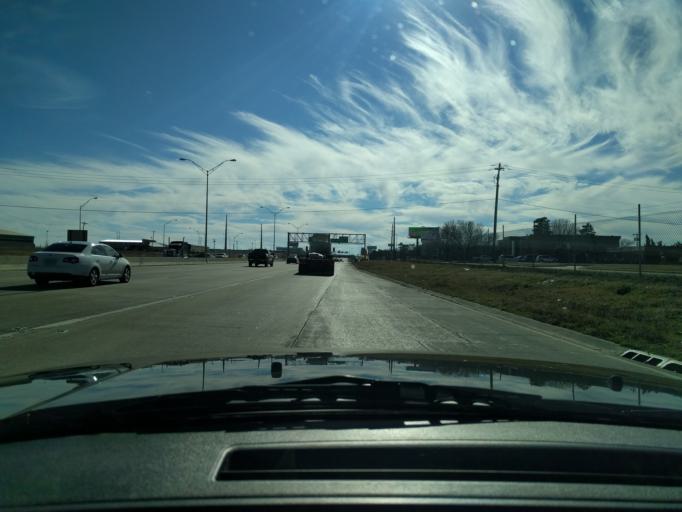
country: US
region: Oklahoma
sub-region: Cleveland County
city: Moore
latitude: 35.3886
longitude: -97.4953
